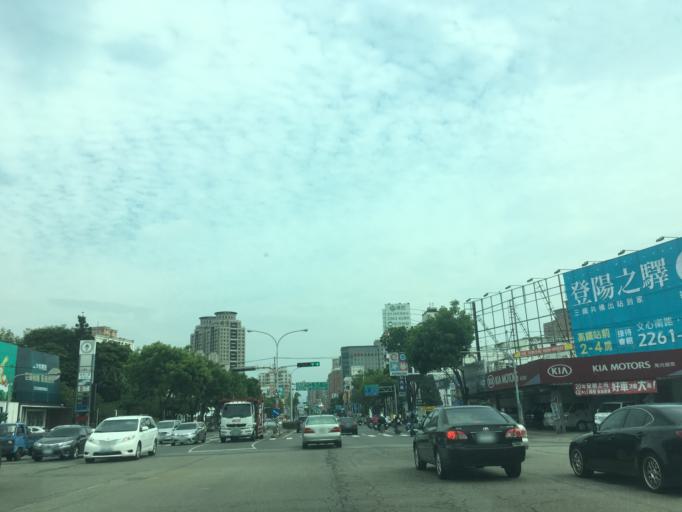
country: TW
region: Taiwan
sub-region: Taichung City
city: Taichung
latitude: 24.1181
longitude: 120.6525
